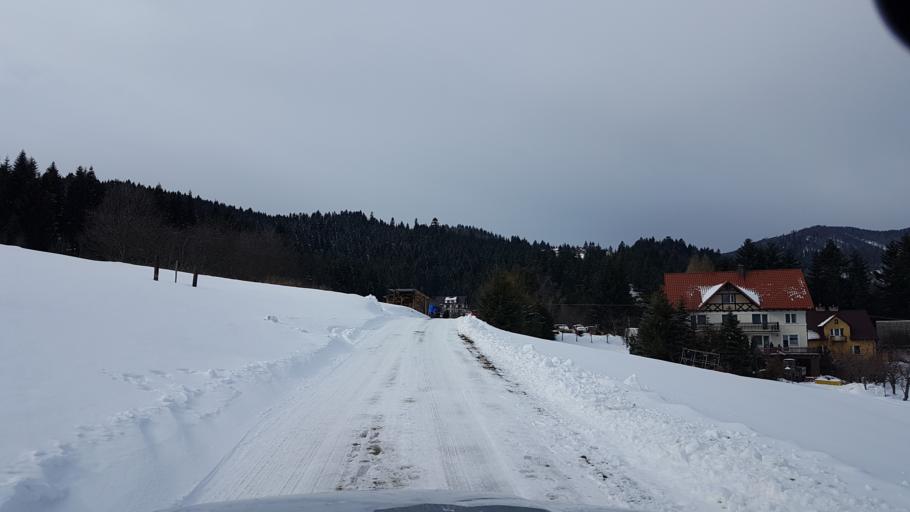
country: PL
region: Lesser Poland Voivodeship
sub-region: Powiat nowosadecki
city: Rytro
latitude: 49.4165
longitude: 20.6363
